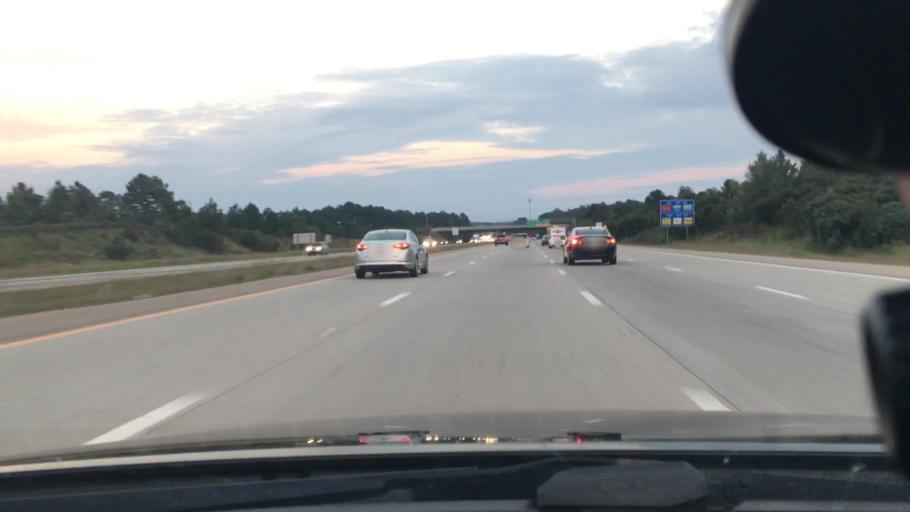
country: US
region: North Carolina
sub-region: Wake County
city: Raleigh
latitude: 35.7795
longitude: -78.5662
